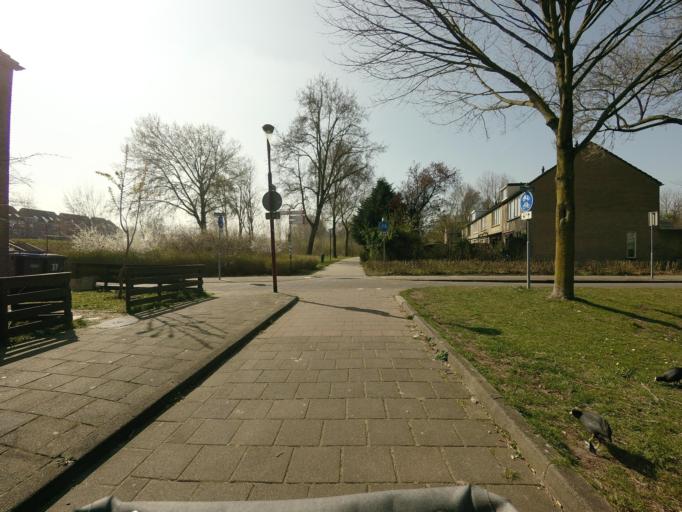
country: NL
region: Utrecht
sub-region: Gemeente Vianen
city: Vianen
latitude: 52.0051
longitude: 5.0809
